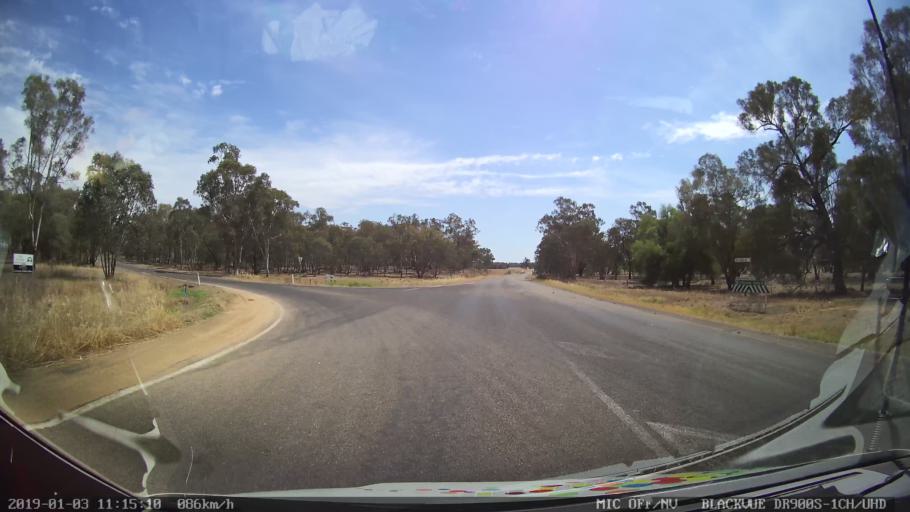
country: AU
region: New South Wales
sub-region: Young
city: Young
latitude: -34.1670
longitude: 148.2625
